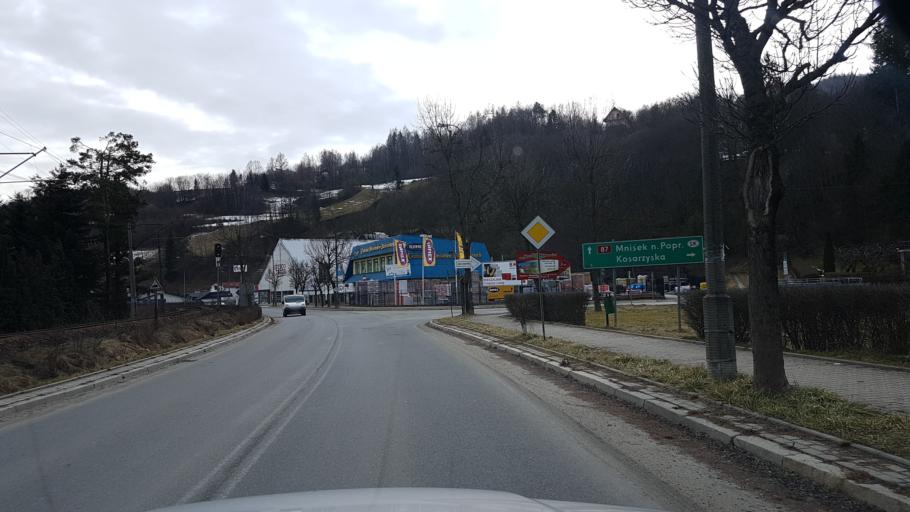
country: PL
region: Lesser Poland Voivodeship
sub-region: Powiat nowosadecki
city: Piwniczna-Zdroj
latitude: 49.4339
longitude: 20.7063
